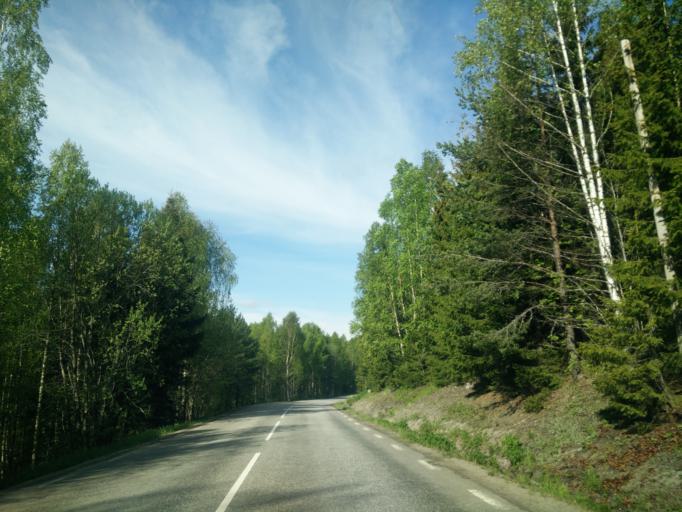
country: SE
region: Vaesternorrland
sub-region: Sundsvalls Kommun
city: Nolby
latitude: 62.3047
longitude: 17.2839
